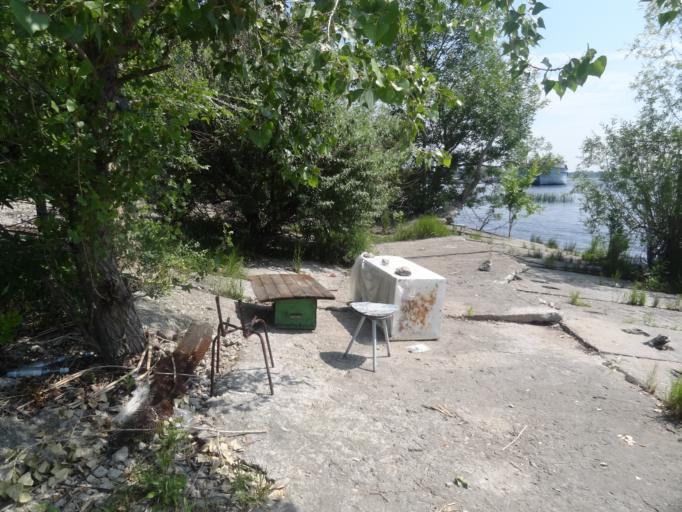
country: RU
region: Saratov
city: Engel's
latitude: 51.5346
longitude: 46.0848
